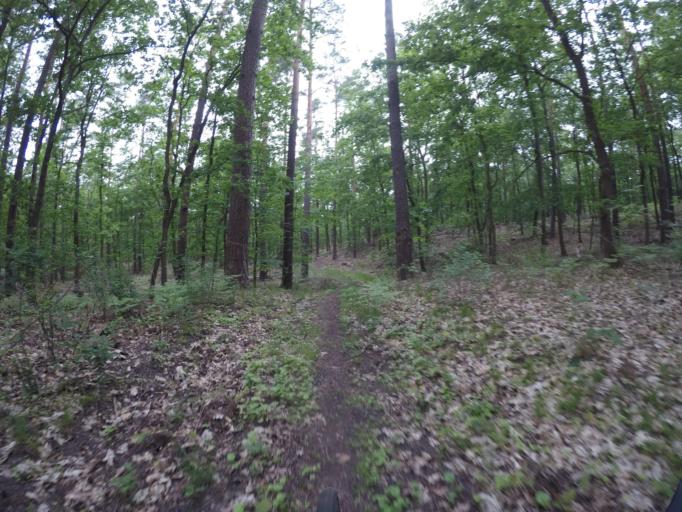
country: DE
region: Berlin
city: Heiligensee
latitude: 52.6249
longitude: 13.2564
